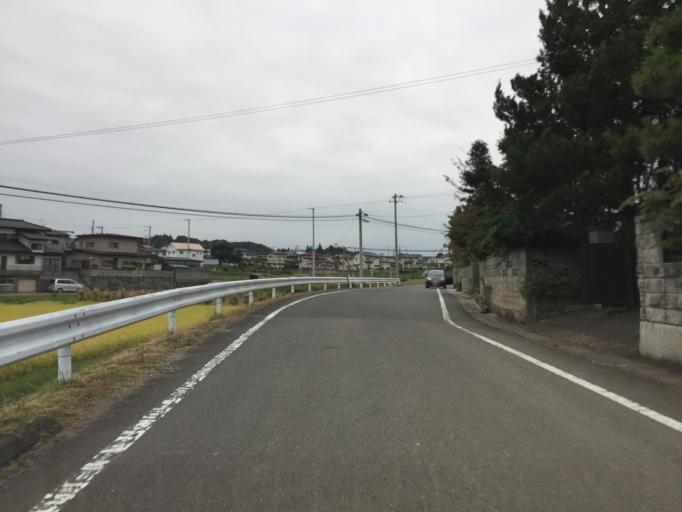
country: JP
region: Fukushima
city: Nihommatsu
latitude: 37.6592
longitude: 140.4747
